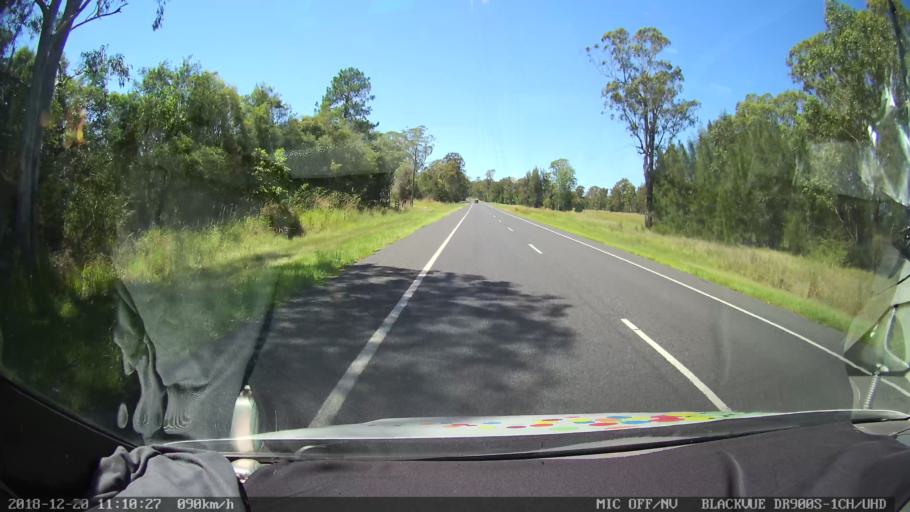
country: AU
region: New South Wales
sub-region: Richmond Valley
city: Casino
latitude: -28.9492
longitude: 153.0091
